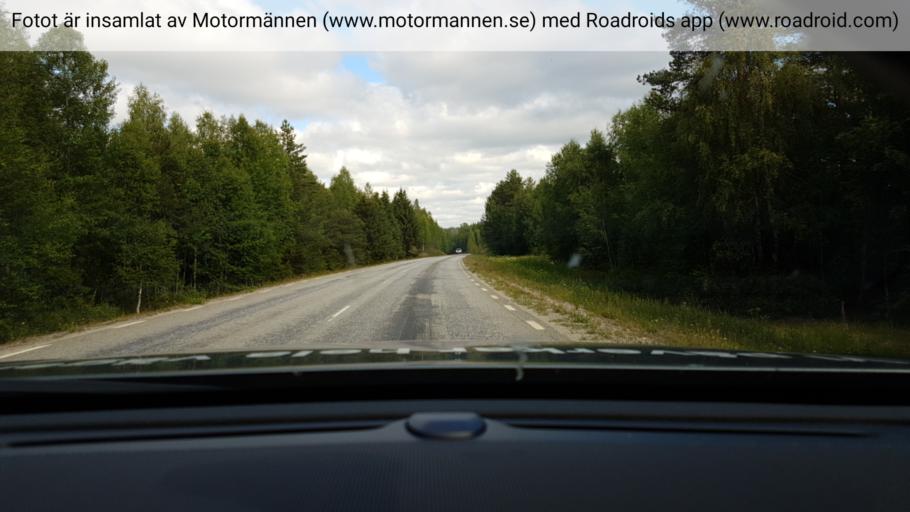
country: SE
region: Vaesterbotten
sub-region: Lycksele Kommun
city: Lycksele
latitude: 64.8441
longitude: 18.7639
